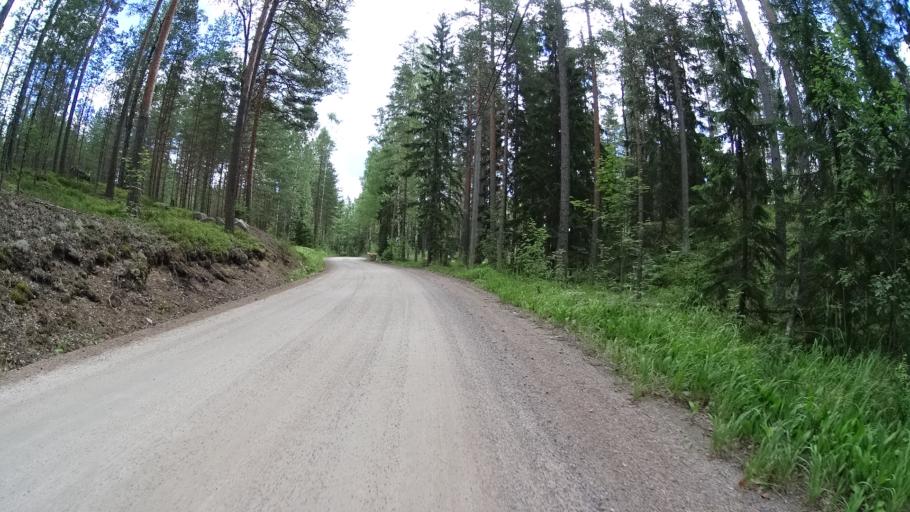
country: FI
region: Uusimaa
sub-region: Helsinki
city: Espoo
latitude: 60.2859
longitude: 24.6052
